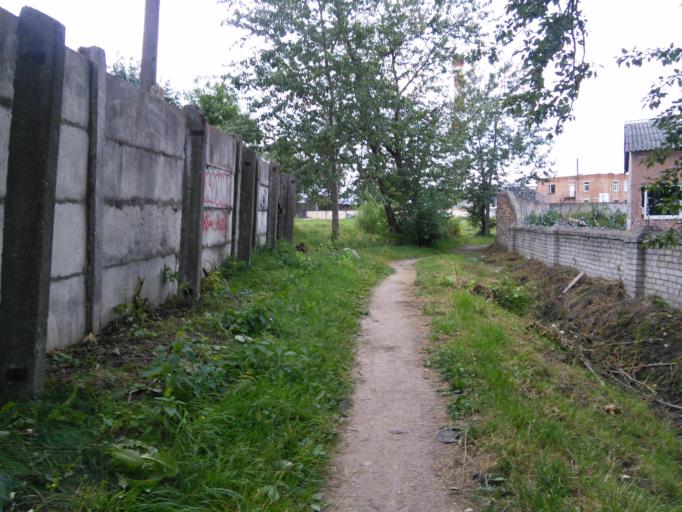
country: BY
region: Minsk
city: Maladzyechna
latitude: 54.3097
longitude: 26.8614
